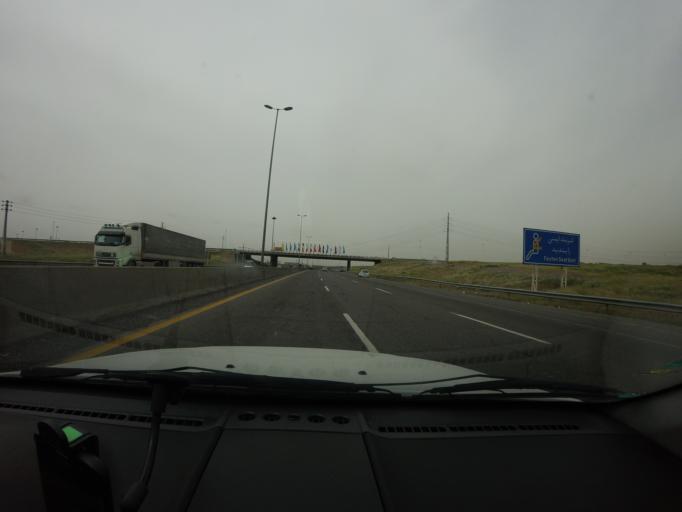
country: IR
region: Tehran
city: Robat Karim
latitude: 35.4720
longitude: 51.0313
